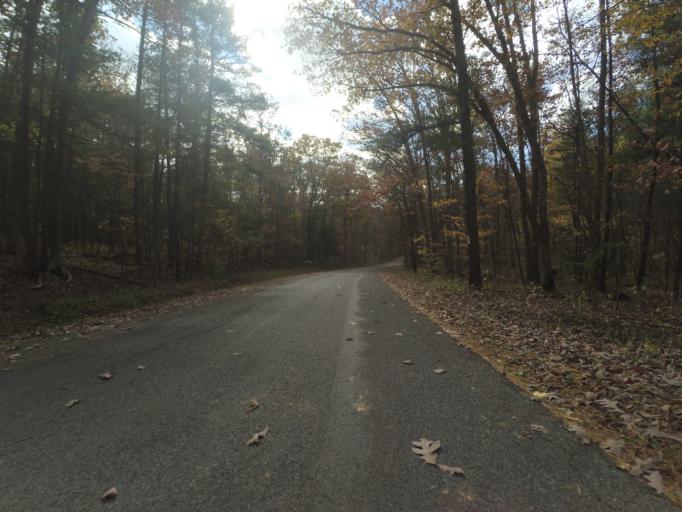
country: US
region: Pennsylvania
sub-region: Centre County
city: Stormstown
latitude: 40.8574
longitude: -77.9775
